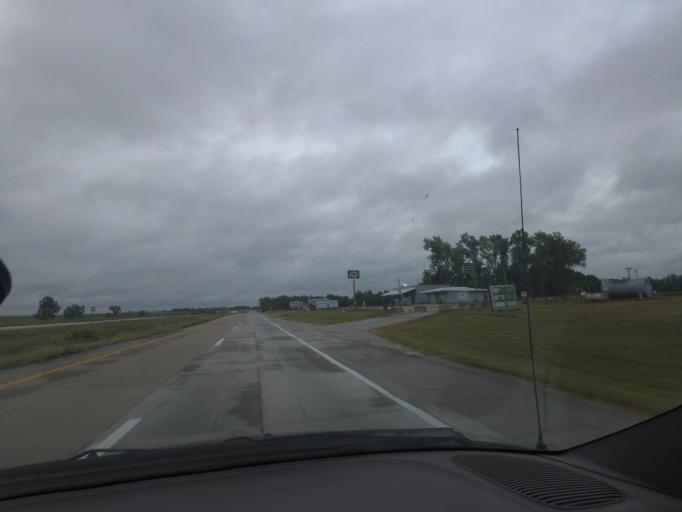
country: US
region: Missouri
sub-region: Marion County
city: Monroe City
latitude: 39.6690
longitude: -91.8535
